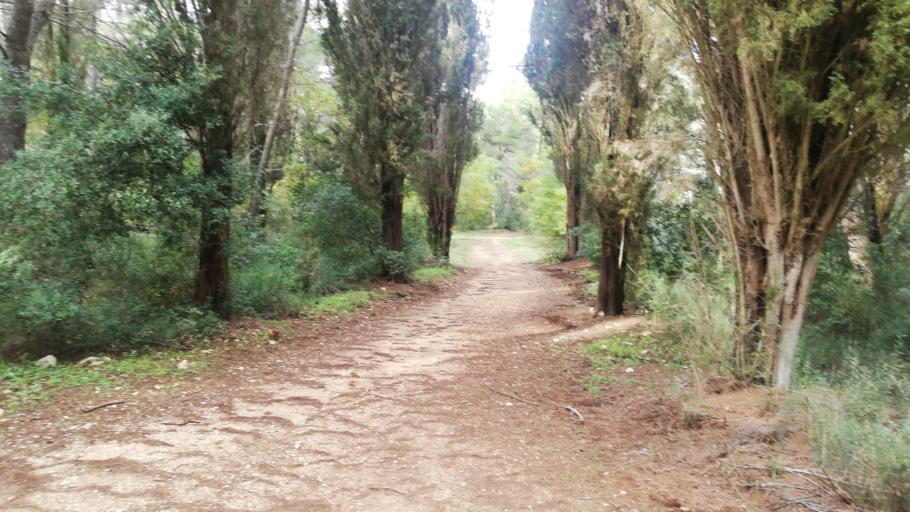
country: IT
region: Apulia
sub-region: Provincia di Bari
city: Cassano delle Murge
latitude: 40.8720
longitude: 16.7141
